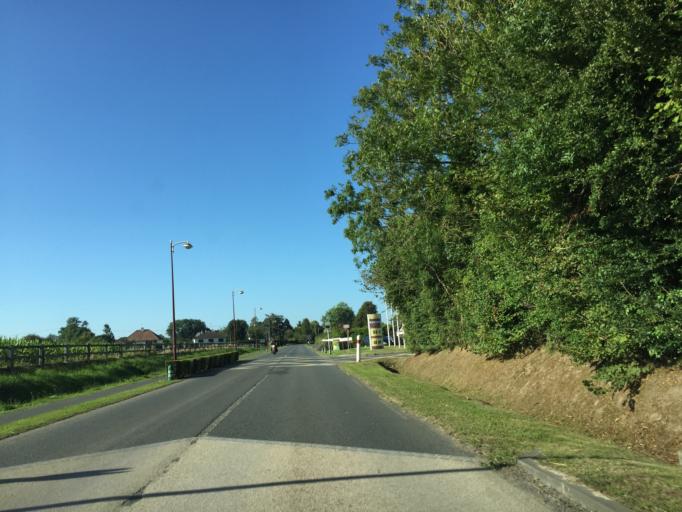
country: FR
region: Lower Normandy
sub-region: Departement du Calvados
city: Equemauville
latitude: 49.3872
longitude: 0.2046
